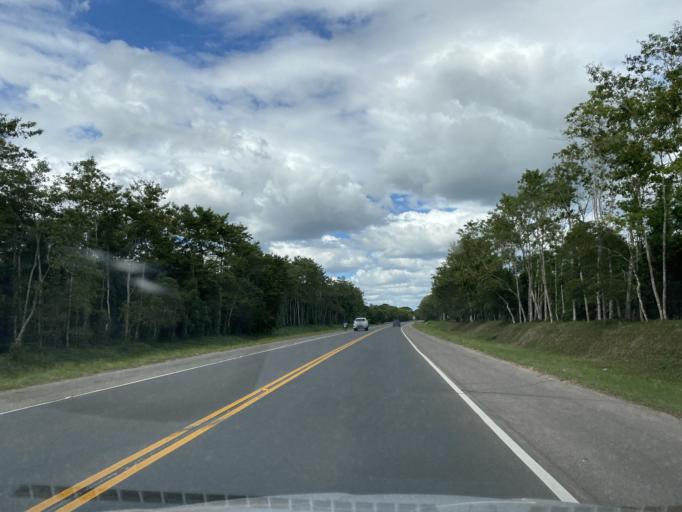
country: DO
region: Santo Domingo
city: Guerra
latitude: 18.5954
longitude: -69.7709
